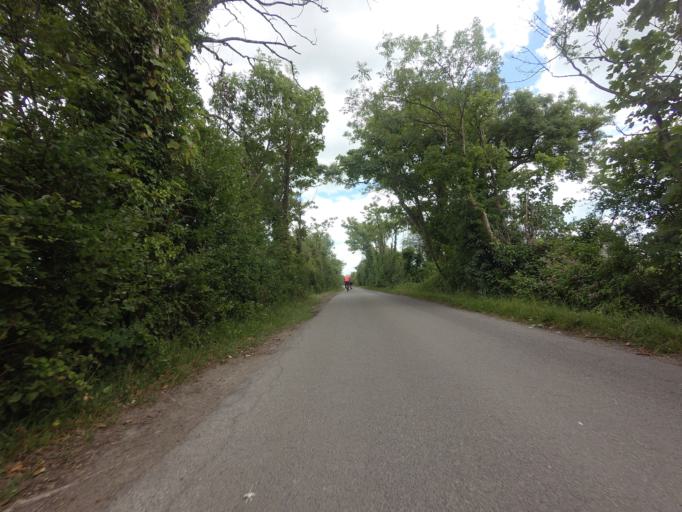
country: GB
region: England
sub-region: East Sussex
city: Pevensey
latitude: 50.8315
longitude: 0.3265
